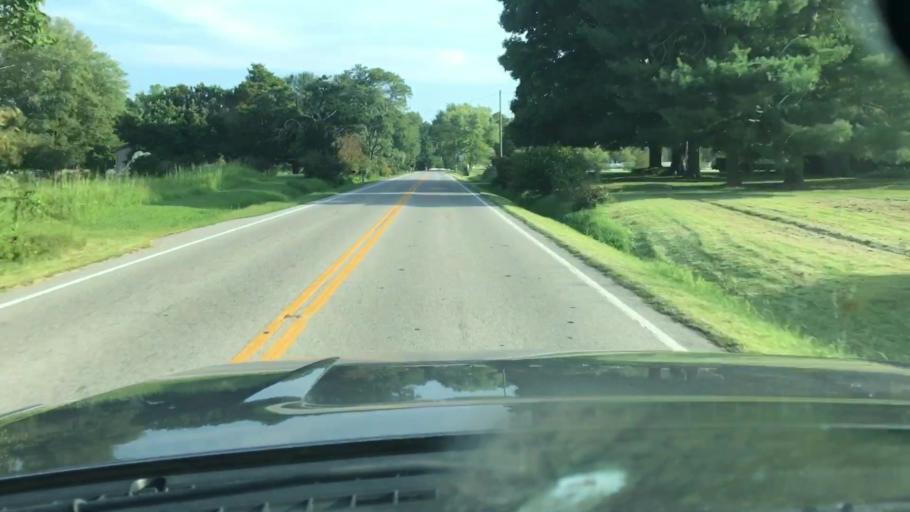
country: US
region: Tennessee
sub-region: Sumner County
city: Portland
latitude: 36.5137
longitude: -86.4241
